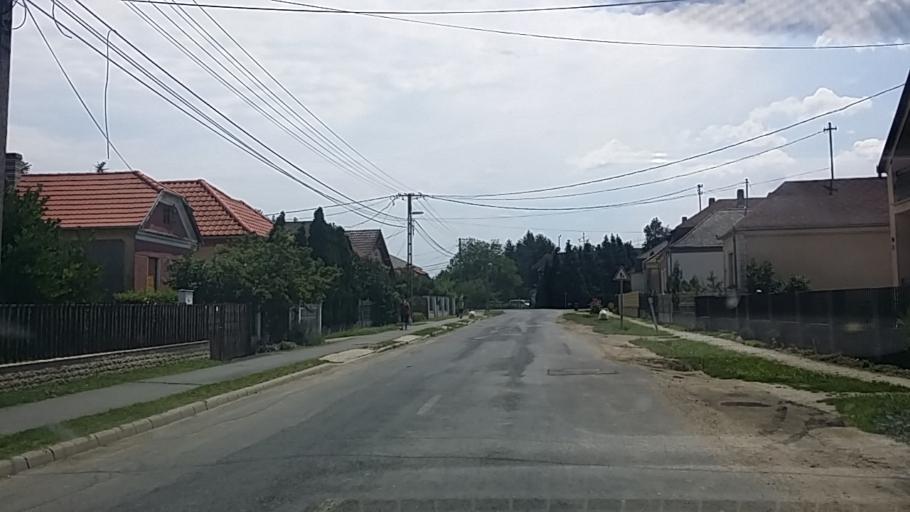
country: HR
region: Medimurska
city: Kotoriba
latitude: 46.3842
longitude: 16.8317
